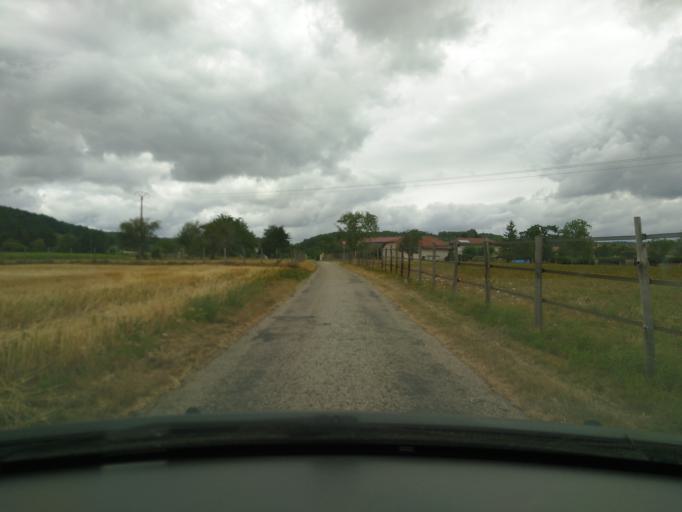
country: FR
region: Rhone-Alpes
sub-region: Departement de l'Isere
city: La Cote-Saint-Andre
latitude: 45.4269
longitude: 5.2215
